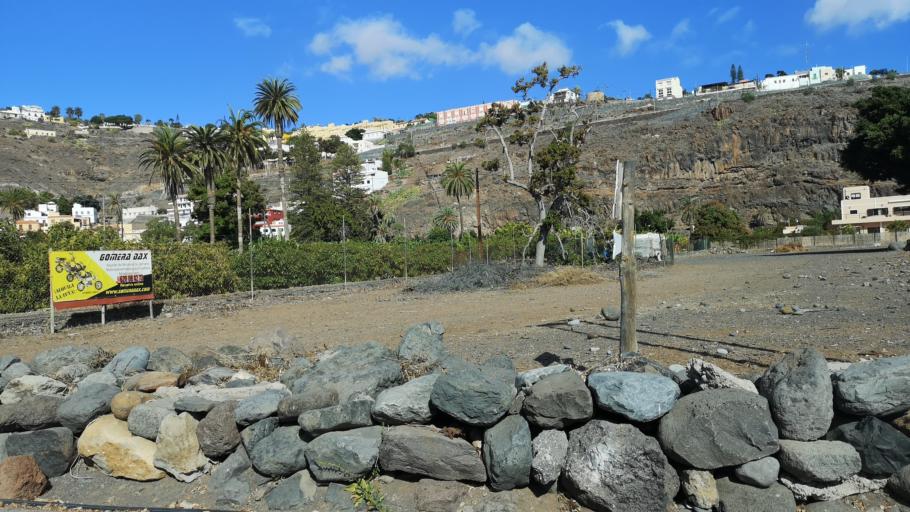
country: ES
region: Canary Islands
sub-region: Provincia de Santa Cruz de Tenerife
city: Alajero
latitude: 28.0298
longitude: -17.1940
